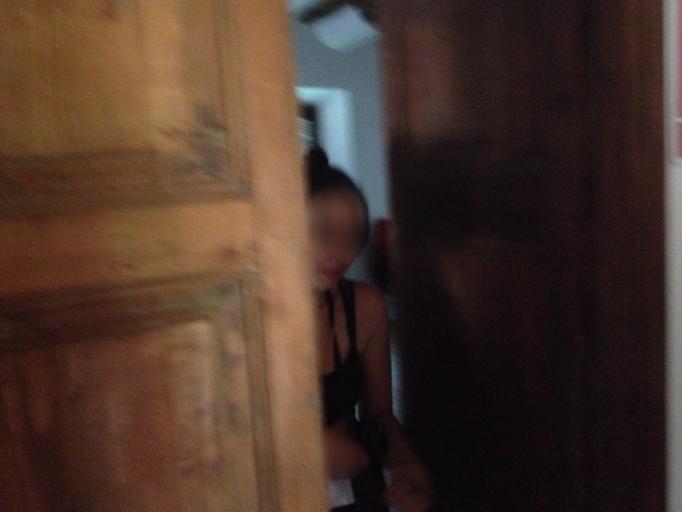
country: IT
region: Latium
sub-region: Citta metropolitana di Roma Capitale
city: Rome
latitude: 41.8653
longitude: 12.5168
